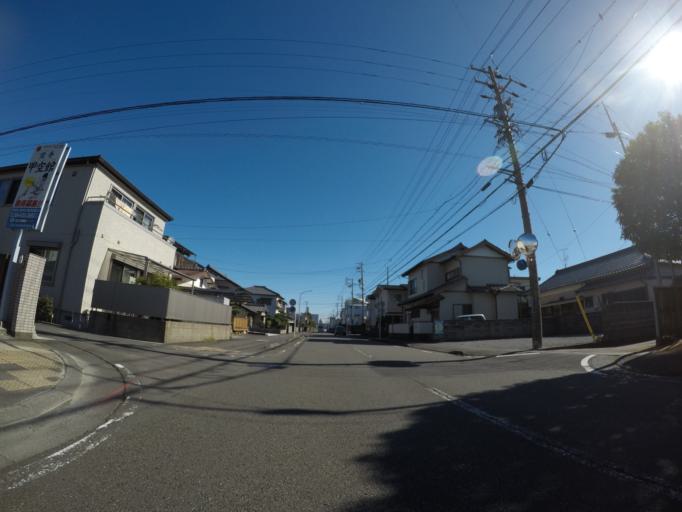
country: JP
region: Shizuoka
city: Fujieda
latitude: 34.8438
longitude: 138.2406
